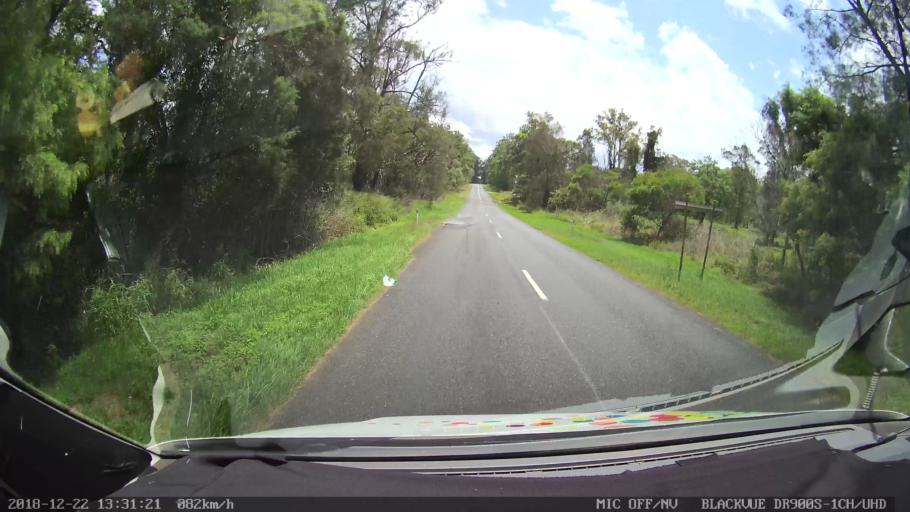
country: AU
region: New South Wales
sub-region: Clarence Valley
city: Coutts Crossing
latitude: -29.8551
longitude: 152.8538
